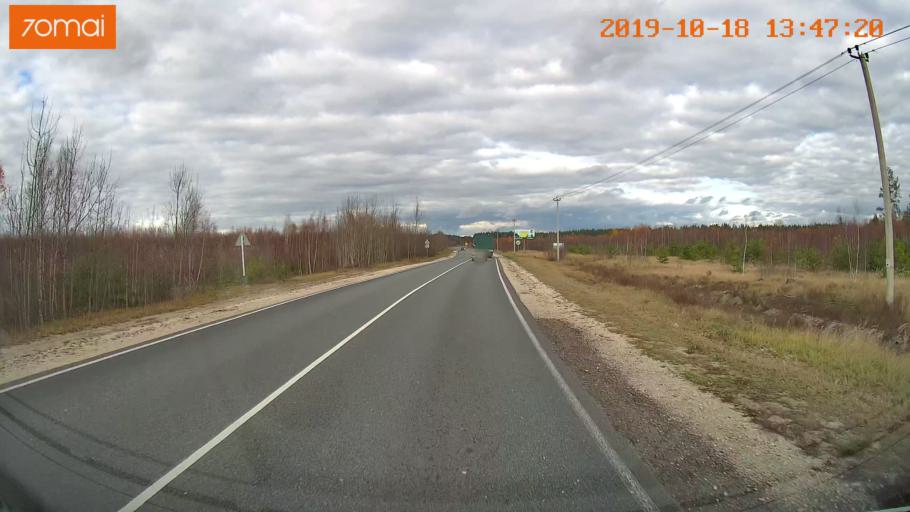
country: RU
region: Rjazan
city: Solotcha
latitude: 54.9730
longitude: 39.9511
